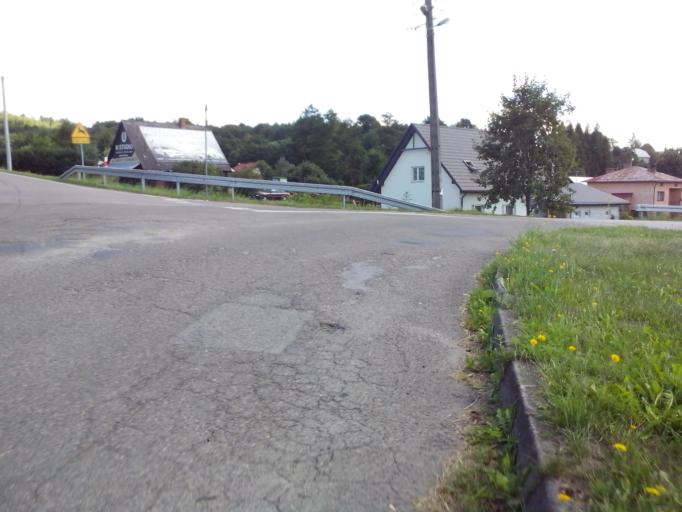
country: PL
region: Subcarpathian Voivodeship
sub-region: Powiat brzozowski
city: Domaradz
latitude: 49.7941
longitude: 21.9484
